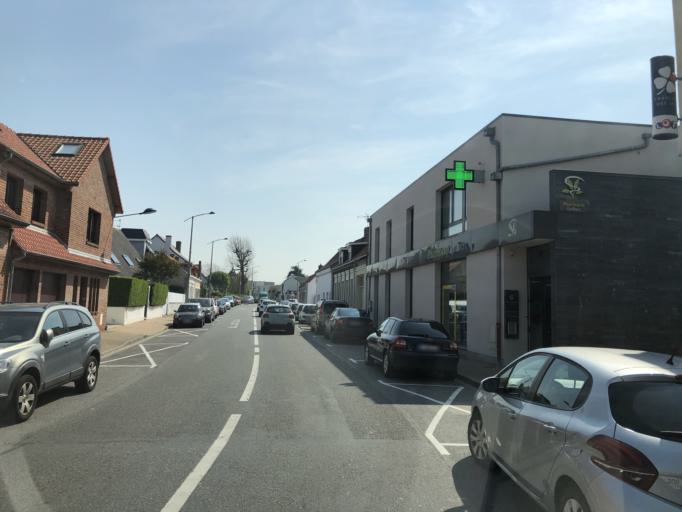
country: FR
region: Nord-Pas-de-Calais
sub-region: Departement du Pas-de-Calais
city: Coquelles
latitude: 50.9345
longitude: 1.7992
